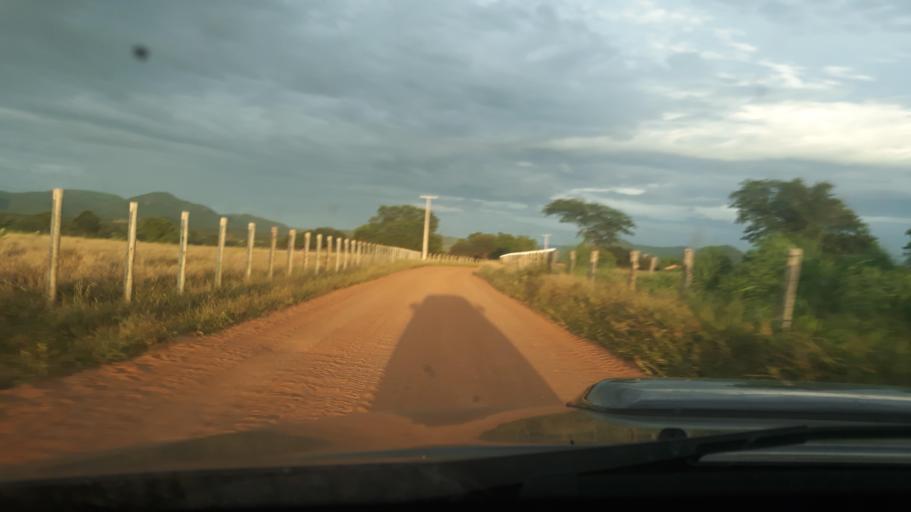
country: BR
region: Bahia
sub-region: Riacho De Santana
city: Riacho de Santana
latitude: -13.9009
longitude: -42.8896
